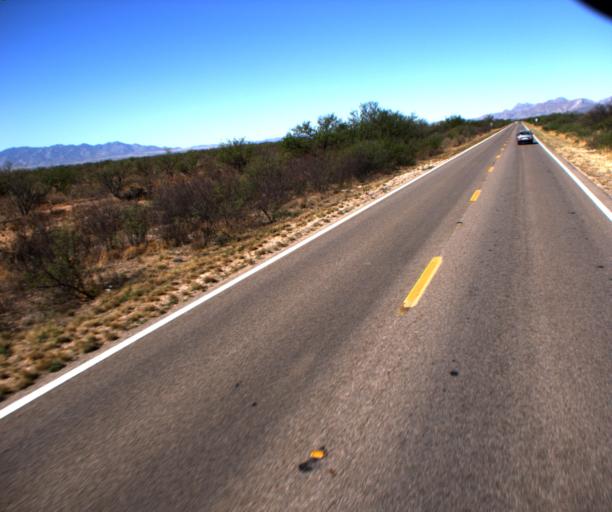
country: US
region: Arizona
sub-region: Cochise County
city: Huachuca City
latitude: 31.7106
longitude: -110.2696
